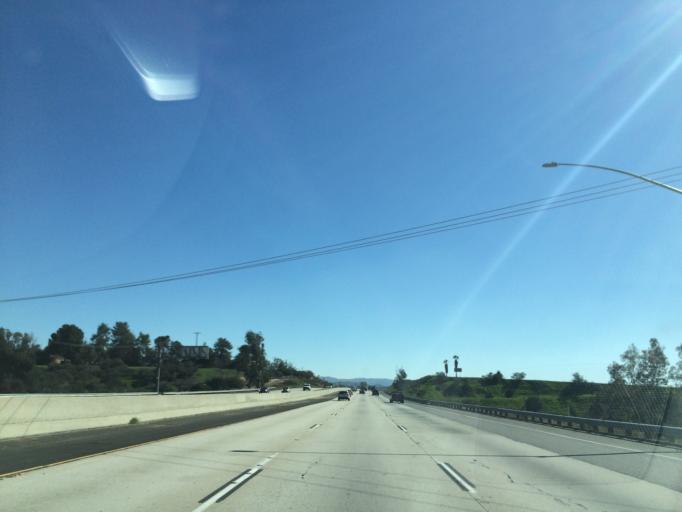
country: US
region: California
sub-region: Riverside County
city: Calimesa
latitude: 33.9901
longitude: -117.0566
